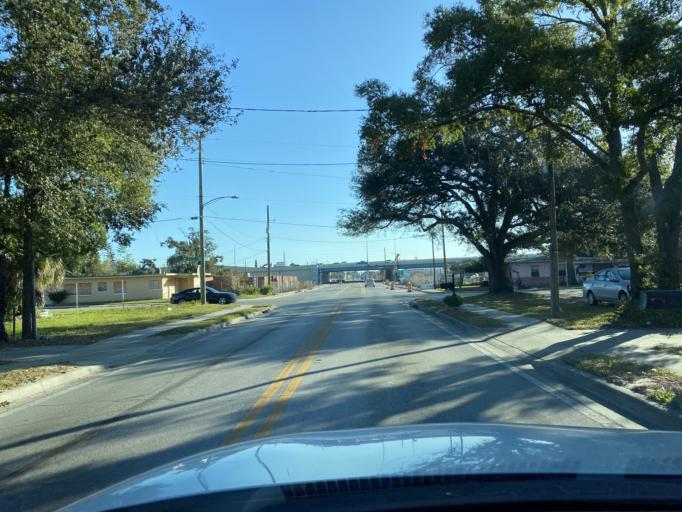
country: US
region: Florida
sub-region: Orange County
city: Orlando
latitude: 28.5201
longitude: -81.3892
